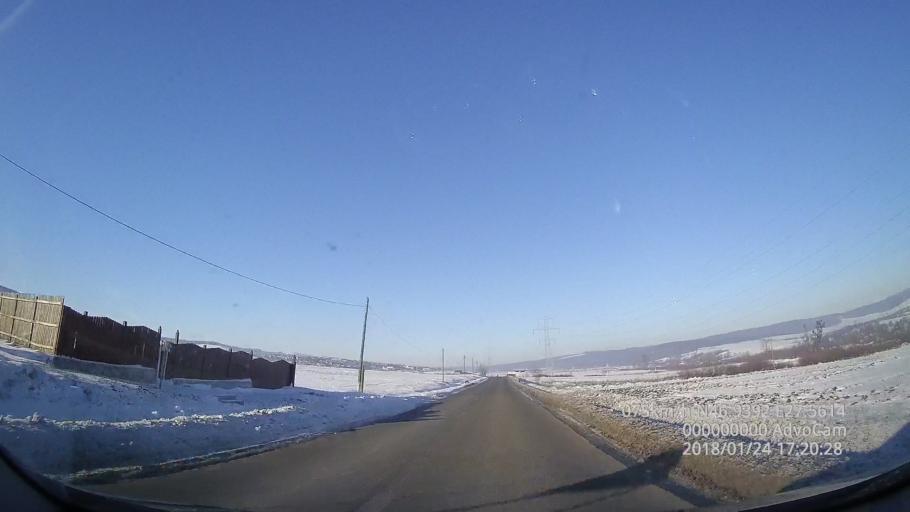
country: RO
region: Iasi
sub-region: Comuna Scanteia
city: Scanteia
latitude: 46.9403
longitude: 27.5612
